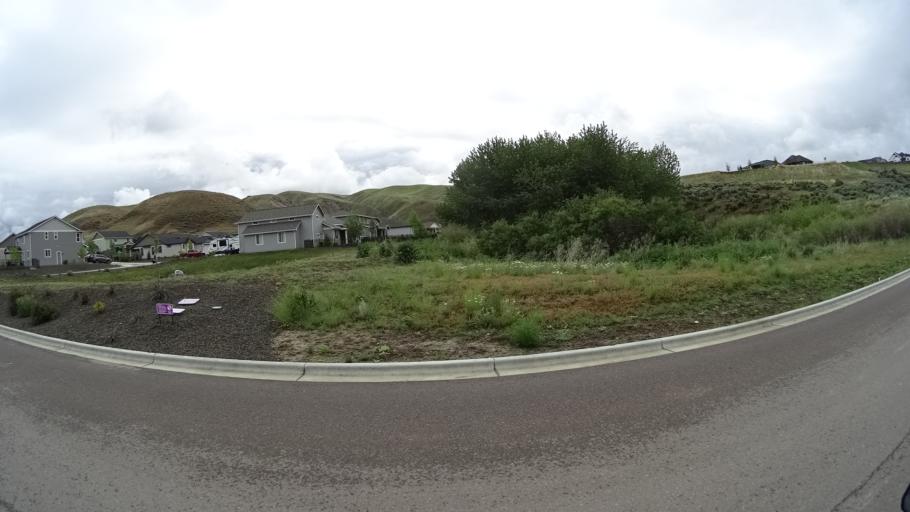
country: US
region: Idaho
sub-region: Ada County
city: Eagle
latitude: 43.7779
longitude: -116.2617
